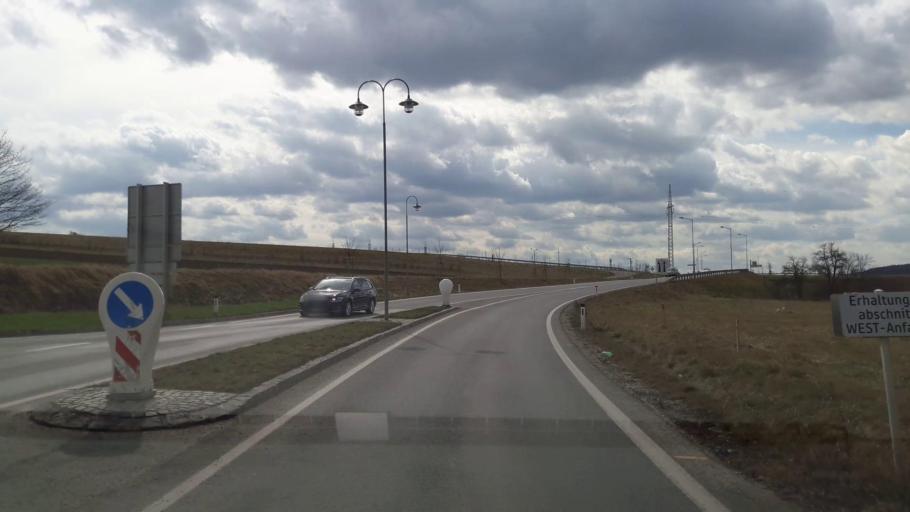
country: AT
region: Lower Austria
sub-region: Politischer Bezirk Mistelbach
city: Mistelbach
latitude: 48.5553
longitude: 16.5621
